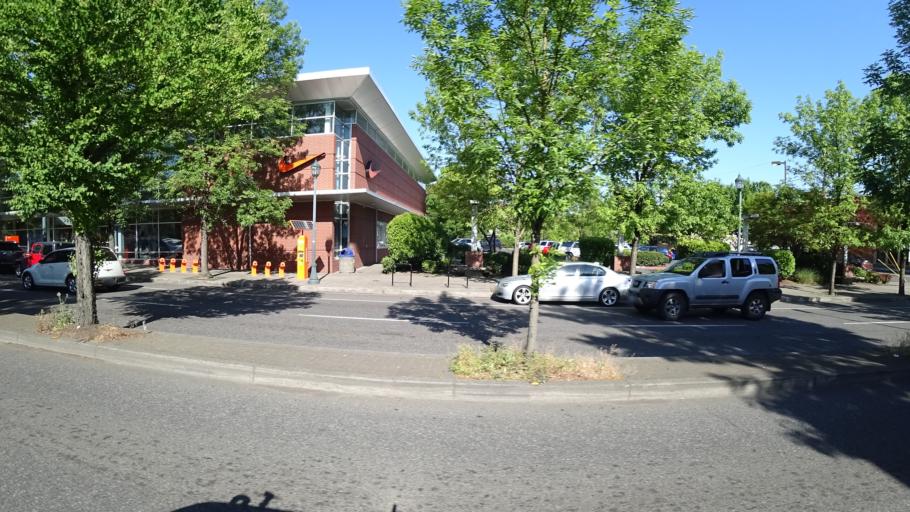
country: US
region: Oregon
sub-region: Multnomah County
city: Portland
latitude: 45.5416
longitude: -122.6616
